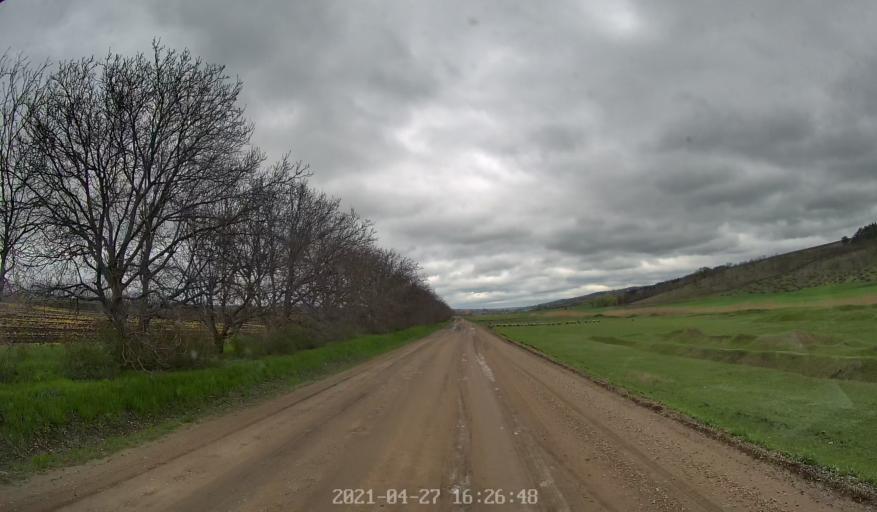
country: MD
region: Chisinau
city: Singera
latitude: 46.9780
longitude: 29.0291
